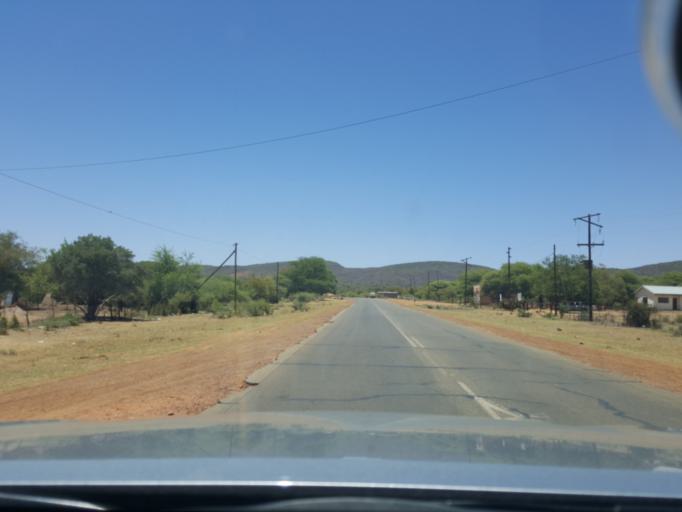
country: BW
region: South East
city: Lobatse
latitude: -25.2896
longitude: 25.9220
